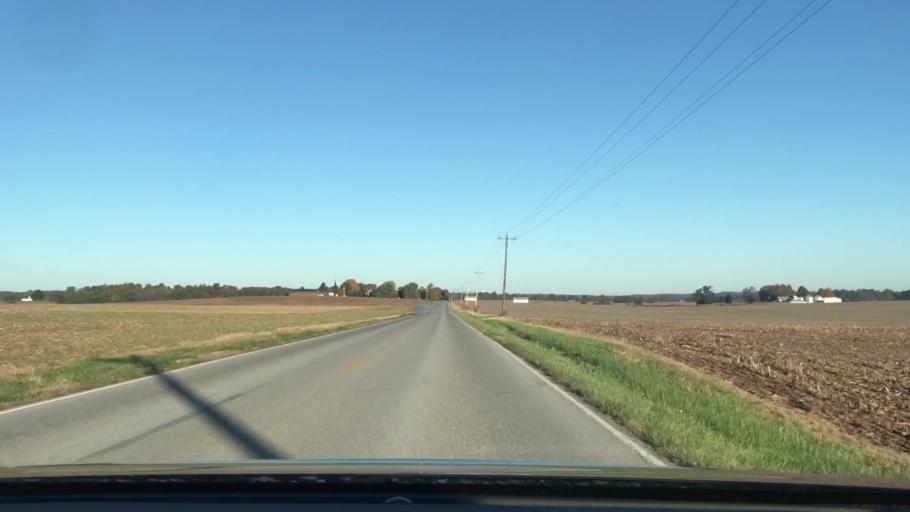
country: US
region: Kentucky
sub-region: Logan County
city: Auburn
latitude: 36.8347
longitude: -86.6874
